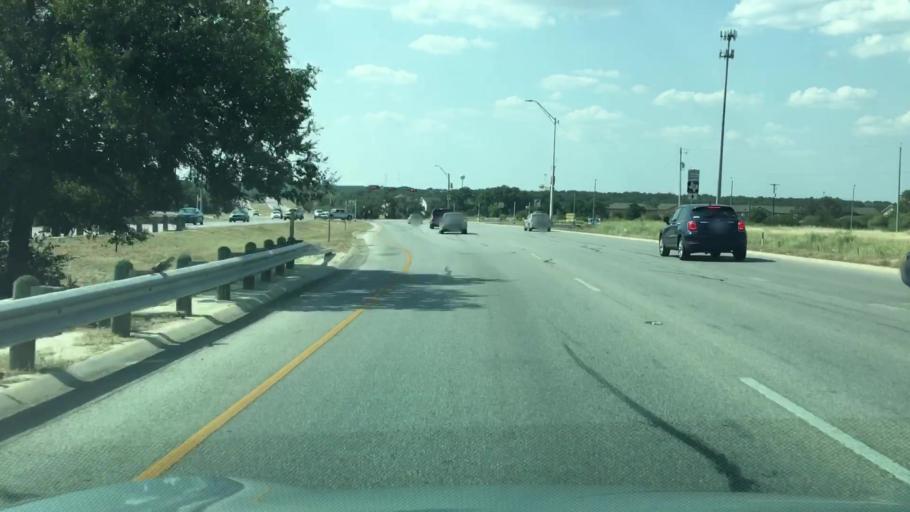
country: US
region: Texas
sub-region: Hays County
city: San Marcos
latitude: 29.8799
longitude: -97.9708
